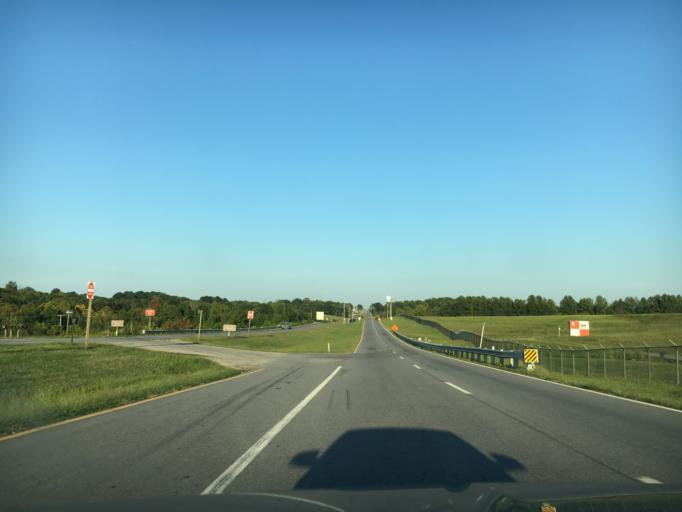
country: US
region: Virginia
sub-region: City of Danville
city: Danville
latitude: 36.5809
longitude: -79.3354
